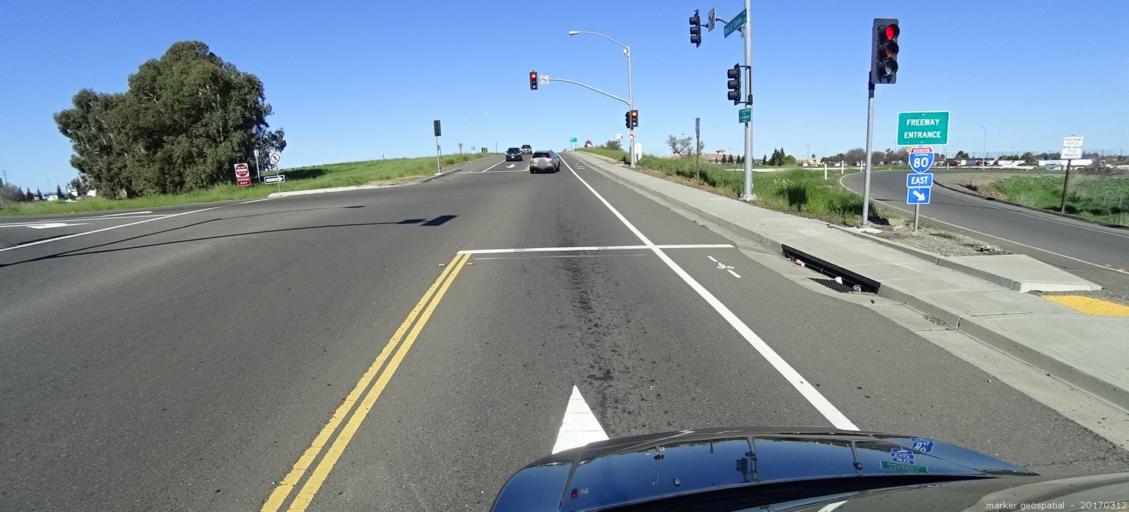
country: US
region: California
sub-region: Yolo County
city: West Sacramento
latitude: 38.6144
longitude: -121.5334
